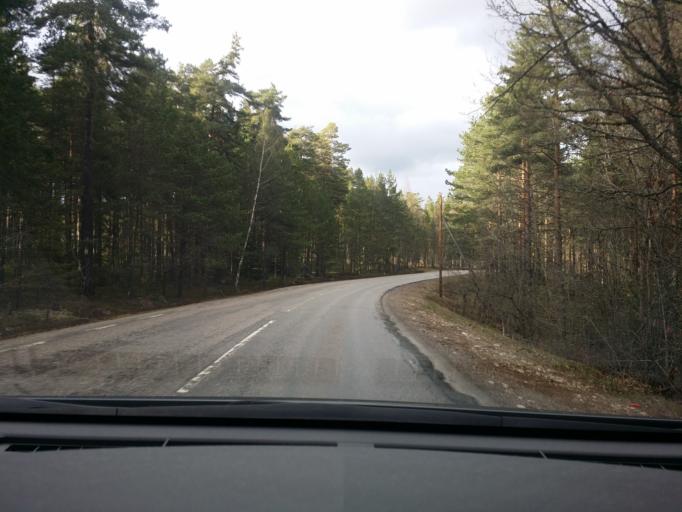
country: SE
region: Soedermanland
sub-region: Eskilstuna Kommun
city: Arla
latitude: 59.3008
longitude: 16.6774
